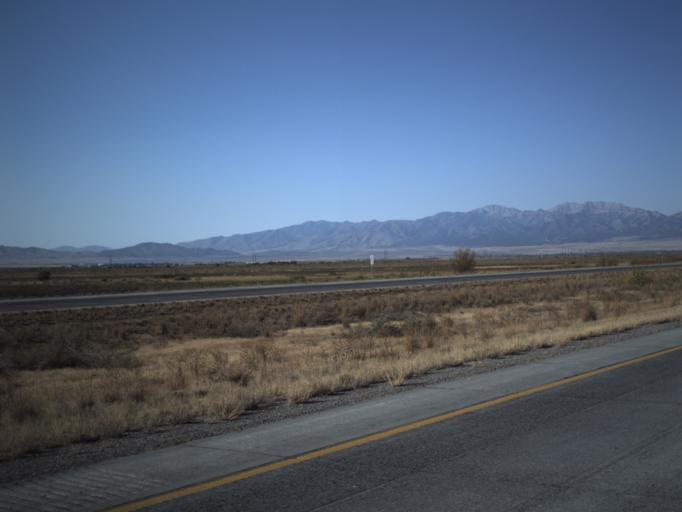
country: US
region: Utah
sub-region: Tooele County
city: Stansbury park
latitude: 40.6645
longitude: -112.3186
